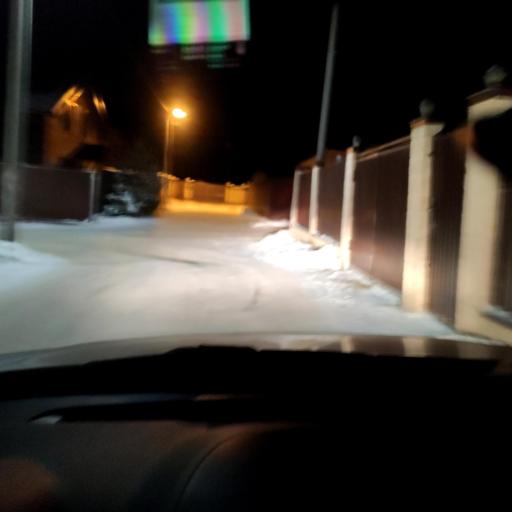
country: RU
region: Tatarstan
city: Vysokaya Gora
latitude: 55.8072
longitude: 49.3857
